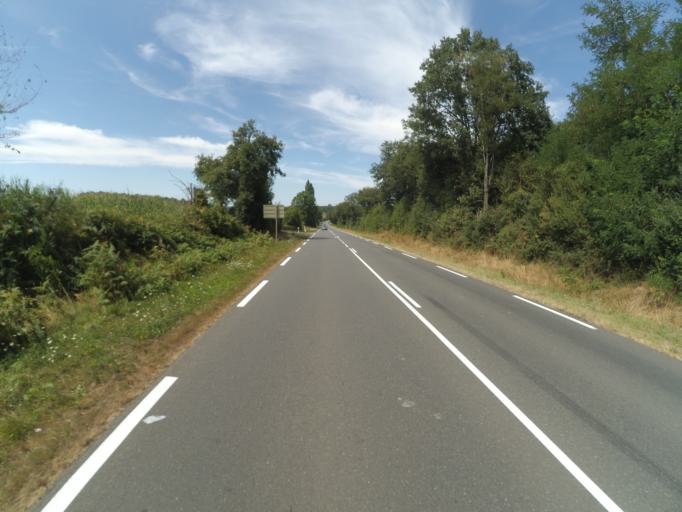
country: FR
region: Poitou-Charentes
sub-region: Departement de la Charente
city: Etagnac
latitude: 45.9233
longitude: 0.7422
